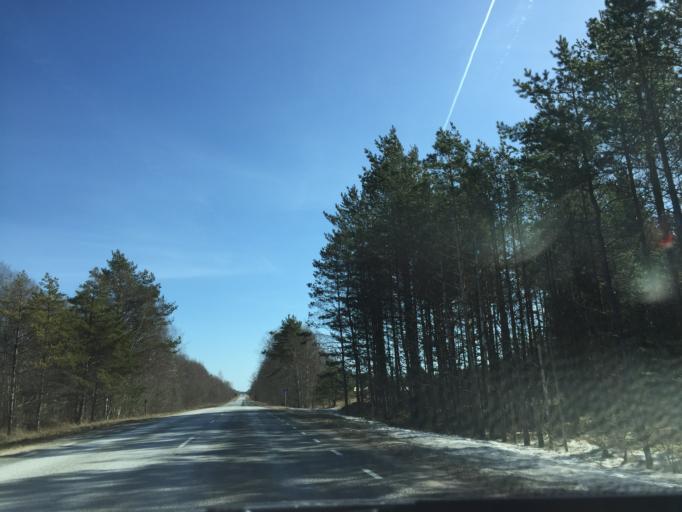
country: EE
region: Laeaene
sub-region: Lihula vald
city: Lihula
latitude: 58.5693
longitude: 23.7567
